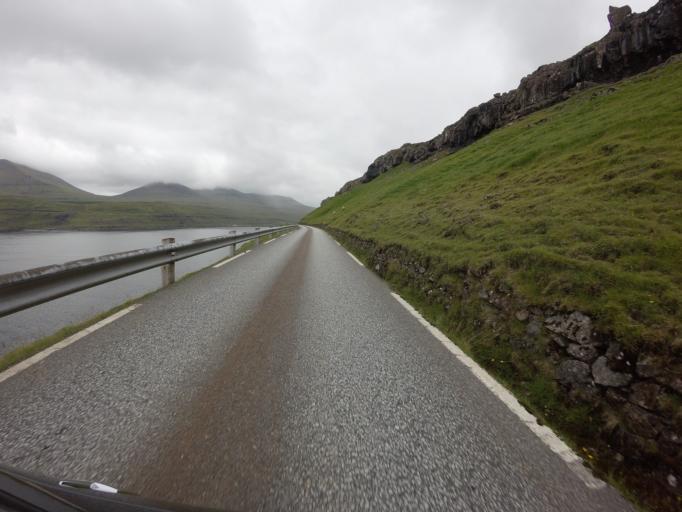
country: FO
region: Eysturoy
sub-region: Eidi
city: Eidi
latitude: 62.2909
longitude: -7.1101
